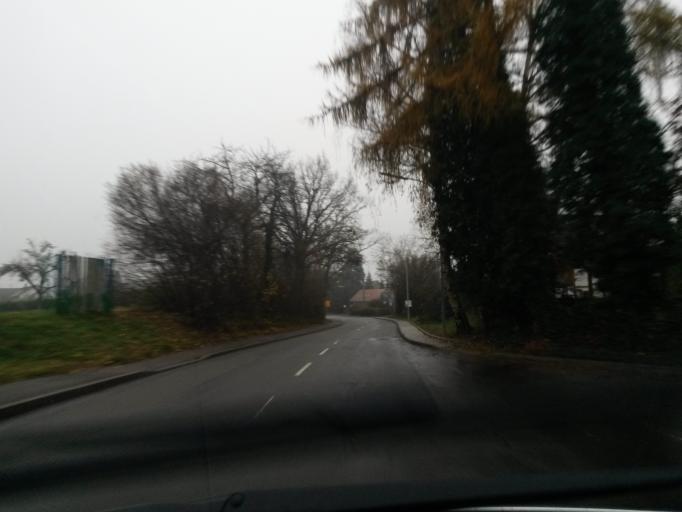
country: DE
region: Baden-Wuerttemberg
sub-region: Karlsruhe Region
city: Altensteig
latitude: 48.6220
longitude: 8.6434
